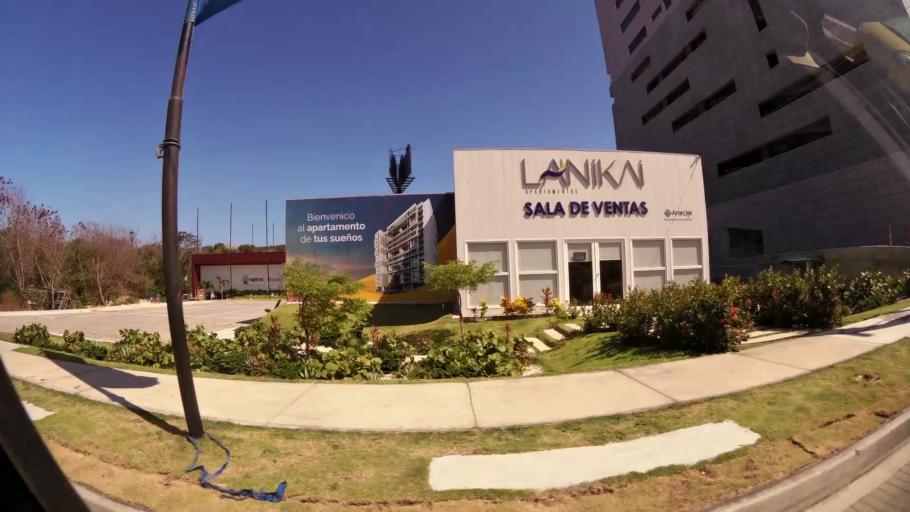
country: CO
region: Atlantico
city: Barranquilla
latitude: 11.0196
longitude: -74.8401
